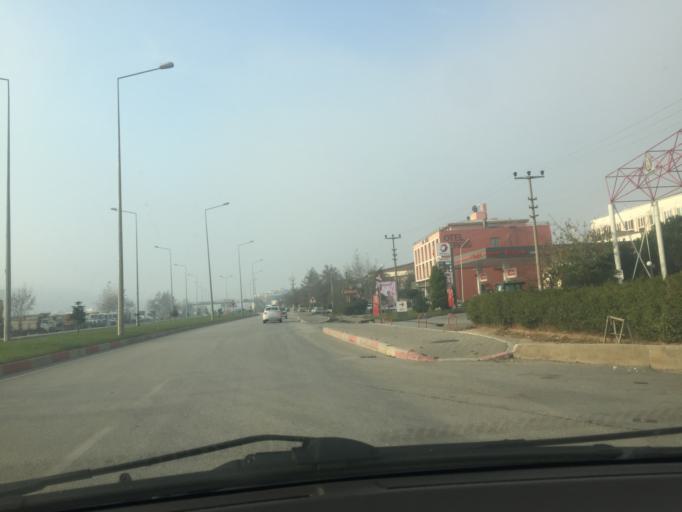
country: TR
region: Canakkale
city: Can
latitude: 40.0283
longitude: 27.0555
